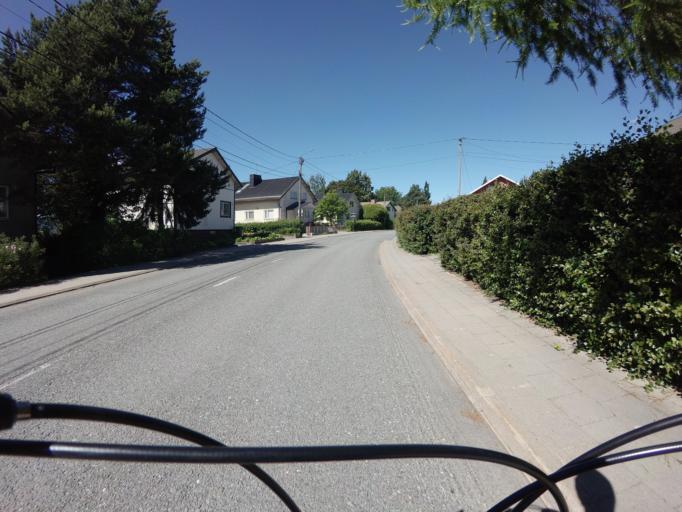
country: FI
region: Varsinais-Suomi
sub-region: Turku
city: Turku
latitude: 60.4561
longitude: 22.2196
